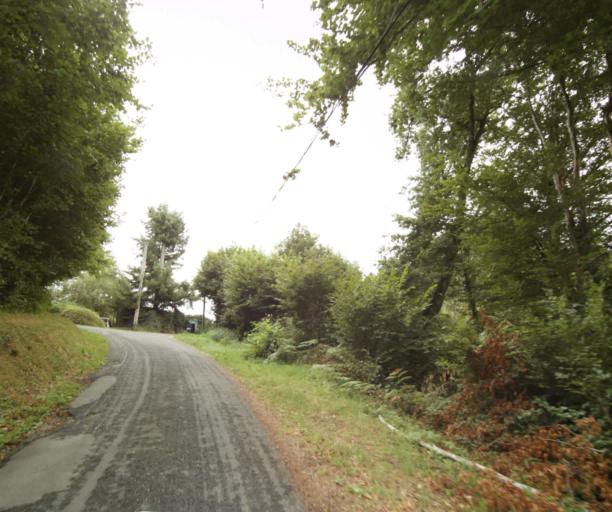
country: FR
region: Limousin
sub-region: Departement de la Correze
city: Sainte-Fortunade
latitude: 45.1800
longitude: 1.8166
